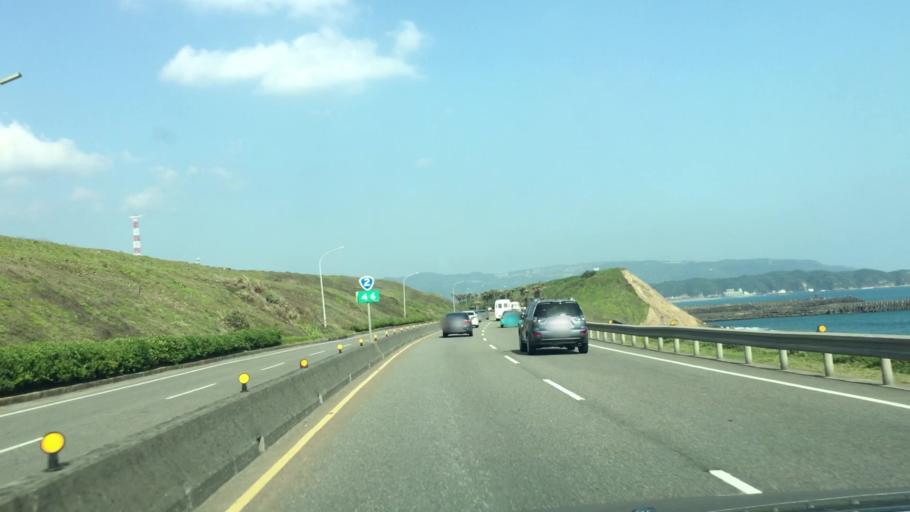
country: TW
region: Taiwan
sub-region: Keelung
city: Keelung
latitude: 25.2035
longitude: 121.6683
